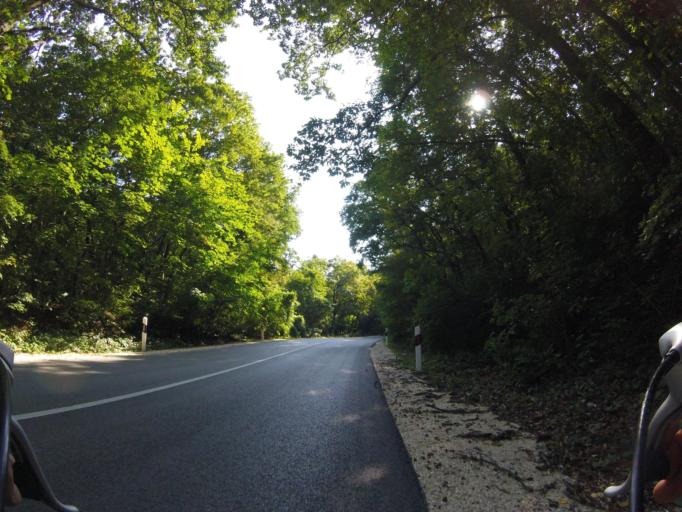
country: HU
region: Komarom-Esztergom
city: Nyergesujfalu
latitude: 47.7046
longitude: 18.5560
